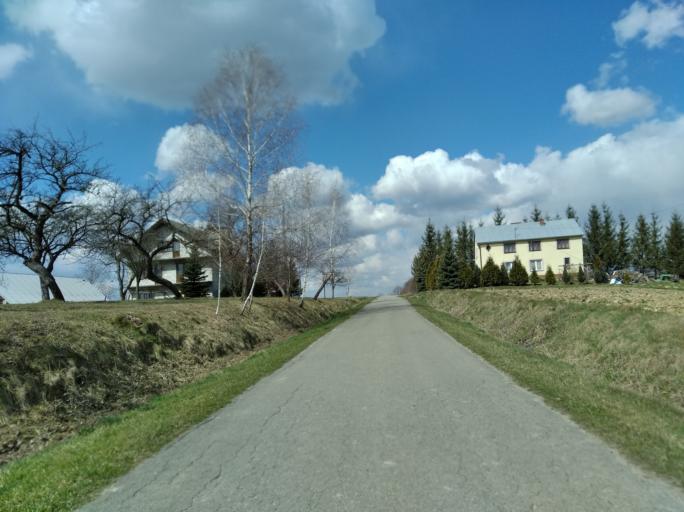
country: PL
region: Subcarpathian Voivodeship
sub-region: Powiat strzyzowski
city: Wisniowa
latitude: 49.9304
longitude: 21.6986
